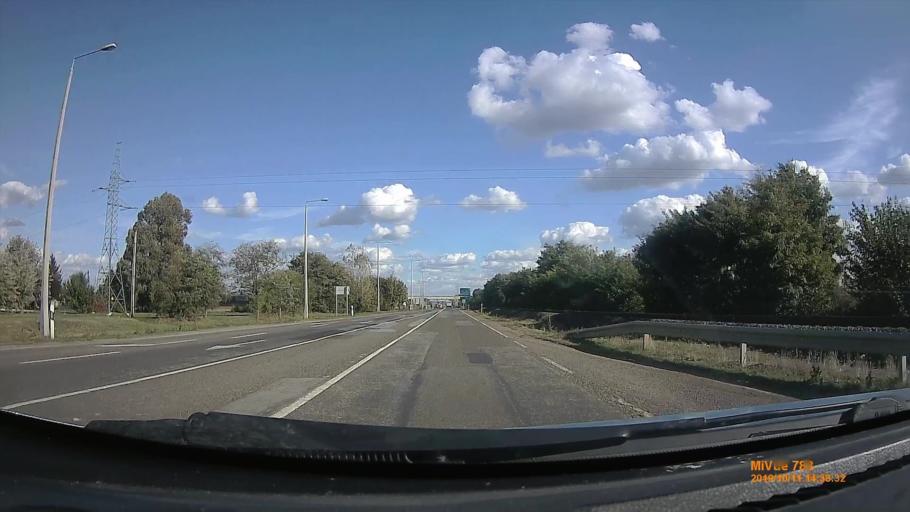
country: HU
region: Hajdu-Bihar
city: Debrecen
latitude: 47.5508
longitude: 21.5432
